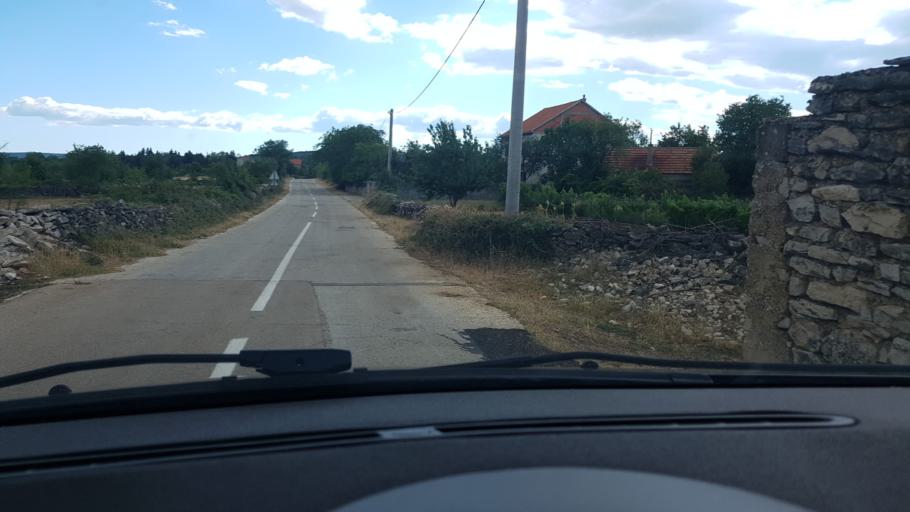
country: HR
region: Sibensko-Kniniska
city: Kistanje
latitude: 44.0553
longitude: 15.9243
